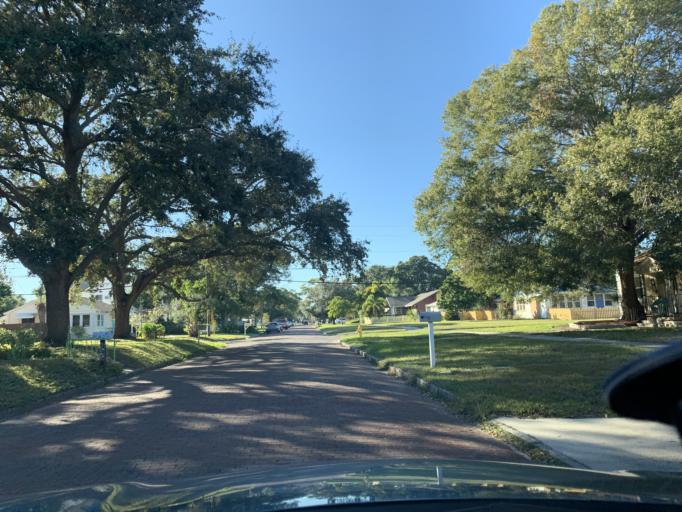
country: US
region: Florida
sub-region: Pinellas County
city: Gulfport
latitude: 27.7435
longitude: -82.7034
